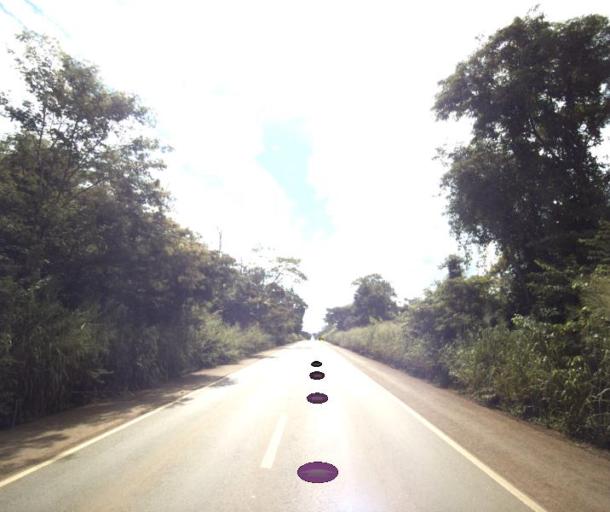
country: BR
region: Goias
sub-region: Petrolina De Goias
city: Petrolina de Goias
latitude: -15.9930
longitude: -49.1497
